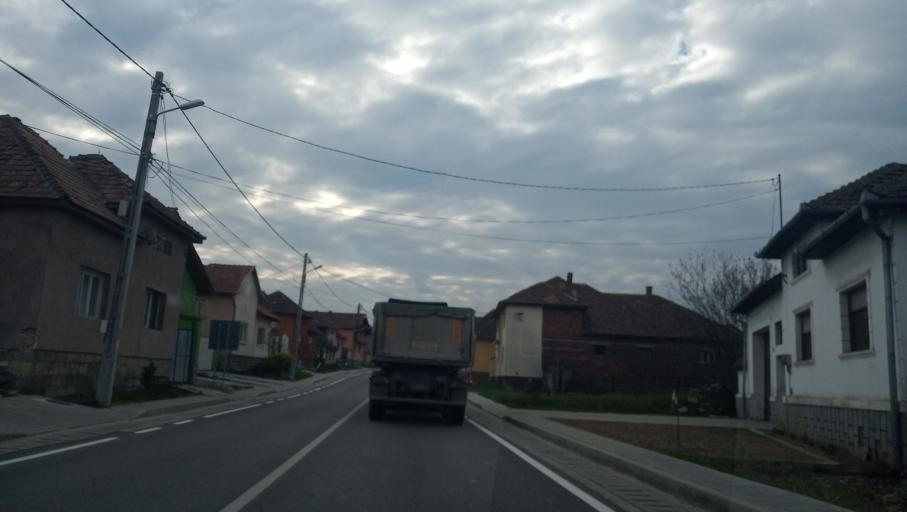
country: RO
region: Bihor
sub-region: Comuna Rieni
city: Ghighiseni
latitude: 46.5478
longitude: 22.4511
